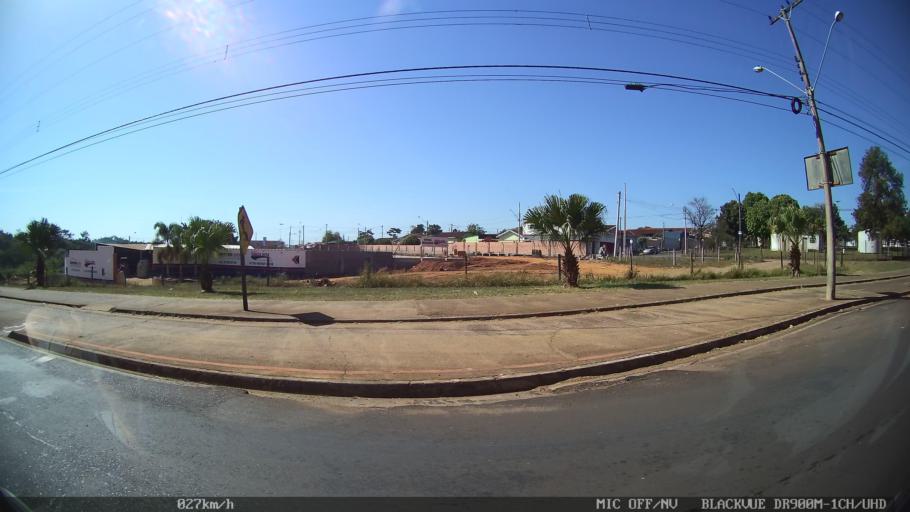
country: BR
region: Sao Paulo
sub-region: Batatais
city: Batatais
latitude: -20.9093
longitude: -47.5826
